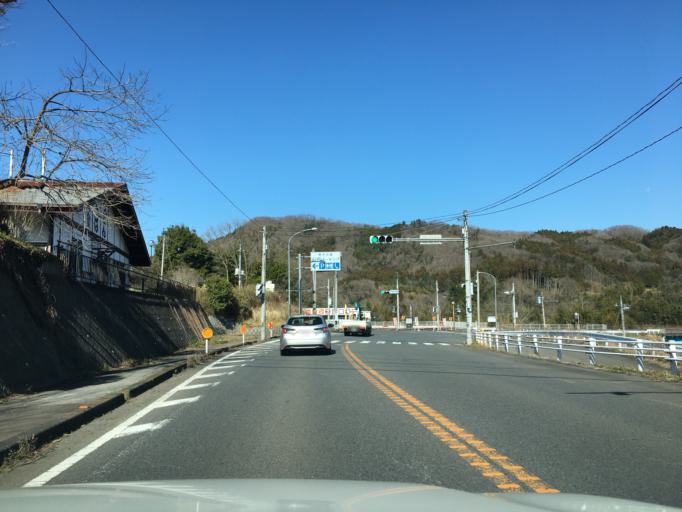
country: JP
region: Tochigi
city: Motegi
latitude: 36.5645
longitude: 140.2436
